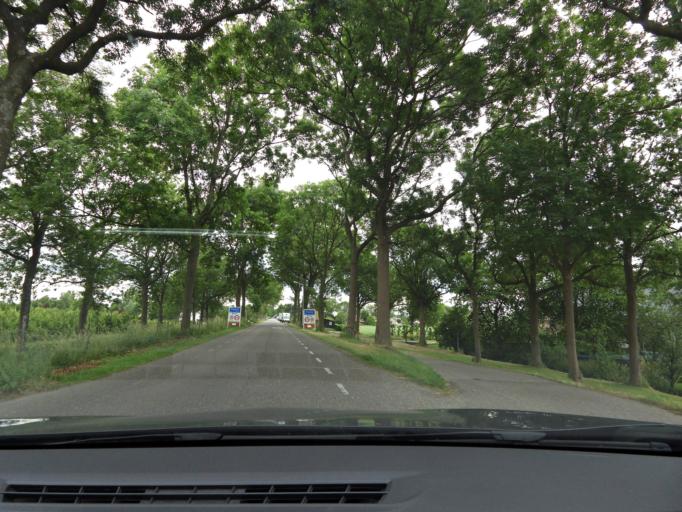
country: NL
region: South Holland
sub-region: Gemeente Oud-Beijerland
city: Oud-Beijerland
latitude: 51.7687
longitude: 4.4310
